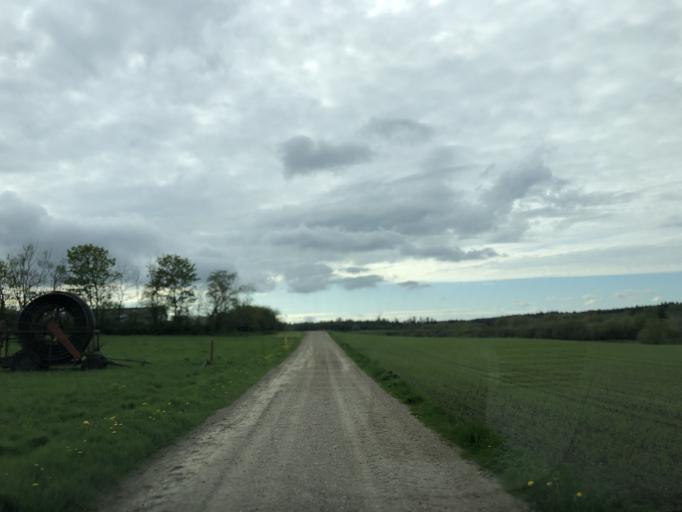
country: DK
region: Central Jutland
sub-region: Holstebro Kommune
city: Ulfborg
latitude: 56.1968
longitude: 8.4539
